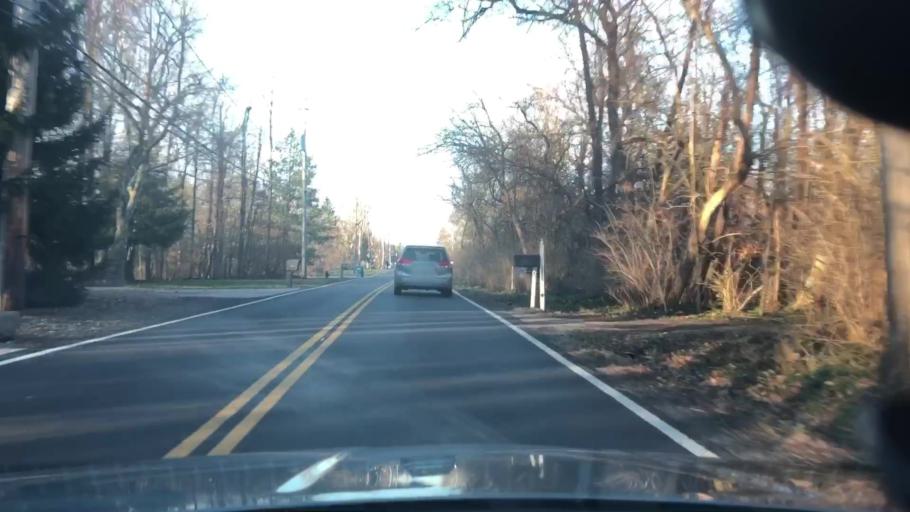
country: US
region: Ohio
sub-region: Cuyahoga County
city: Olmsted Falls
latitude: 41.3696
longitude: -81.8959
